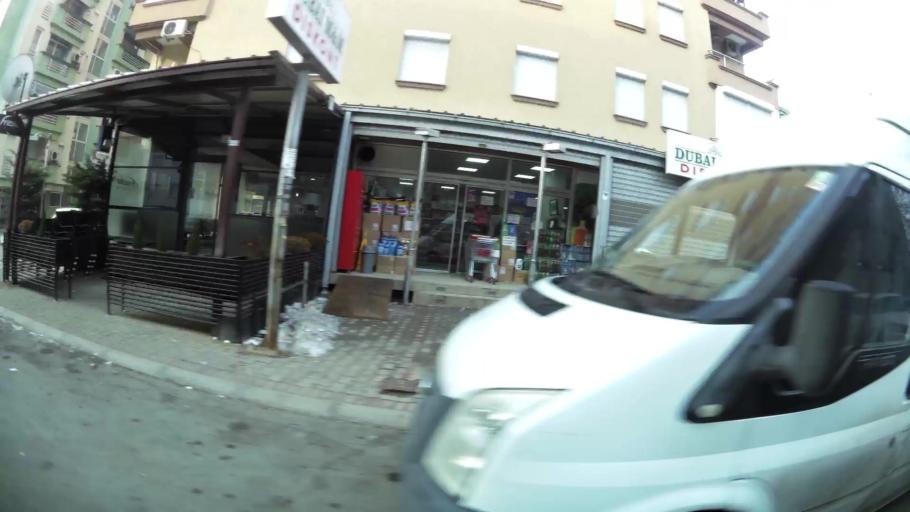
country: MK
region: Cair
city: Cair
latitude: 42.0176
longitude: 21.4454
